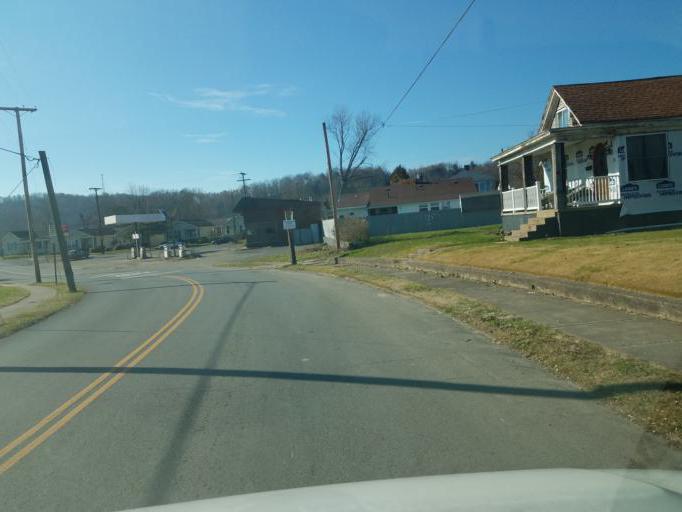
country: US
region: Ohio
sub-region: Scioto County
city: Sciotodale
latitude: 38.7669
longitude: -82.8875
